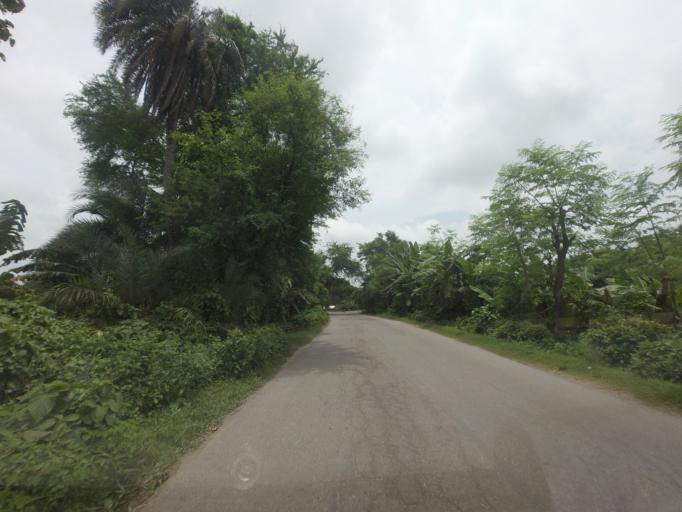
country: BD
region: Khulna
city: Kalia
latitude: 23.2100
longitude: 89.7081
